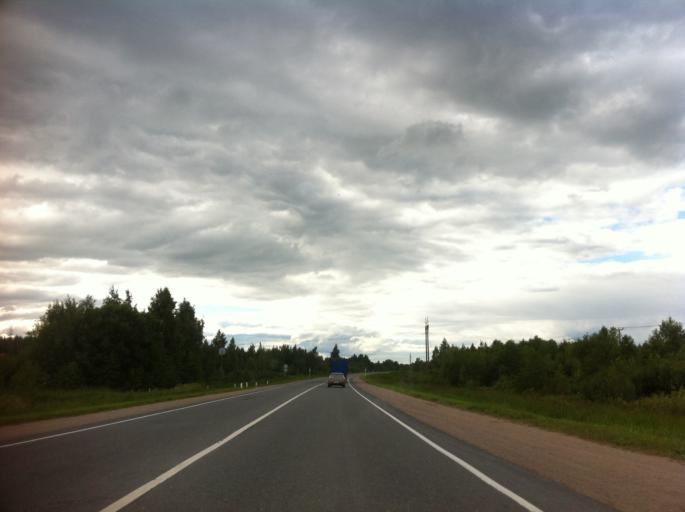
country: RU
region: Pskov
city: Pskov
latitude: 57.8384
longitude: 28.4075
